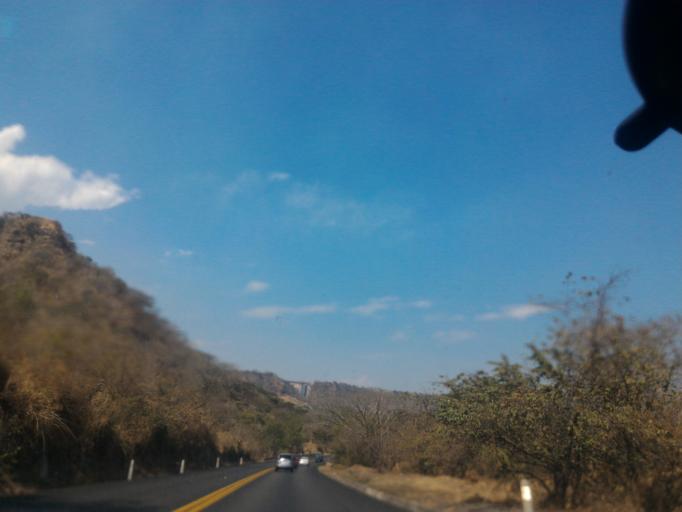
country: MX
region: Jalisco
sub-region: Tonila
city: San Marcos
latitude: 19.4657
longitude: -103.4648
